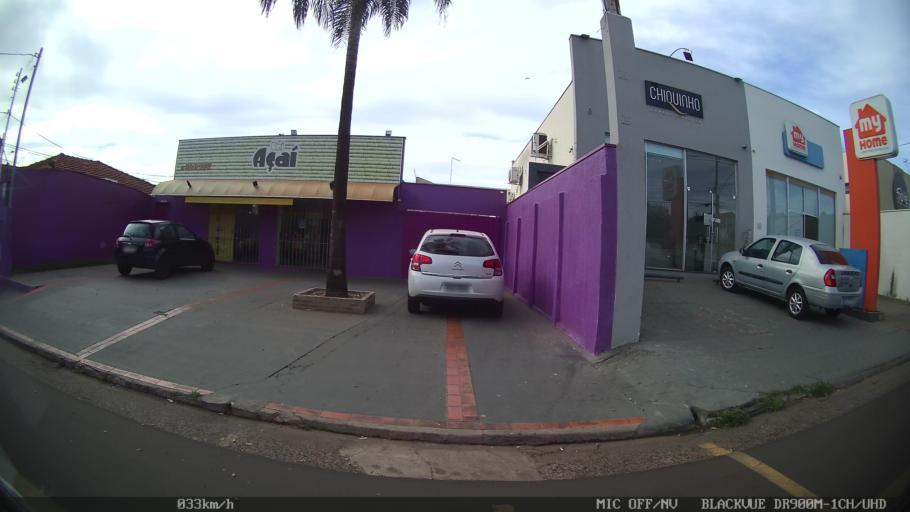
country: BR
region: Sao Paulo
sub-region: Catanduva
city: Catanduva
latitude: -21.1382
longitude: -48.9804
